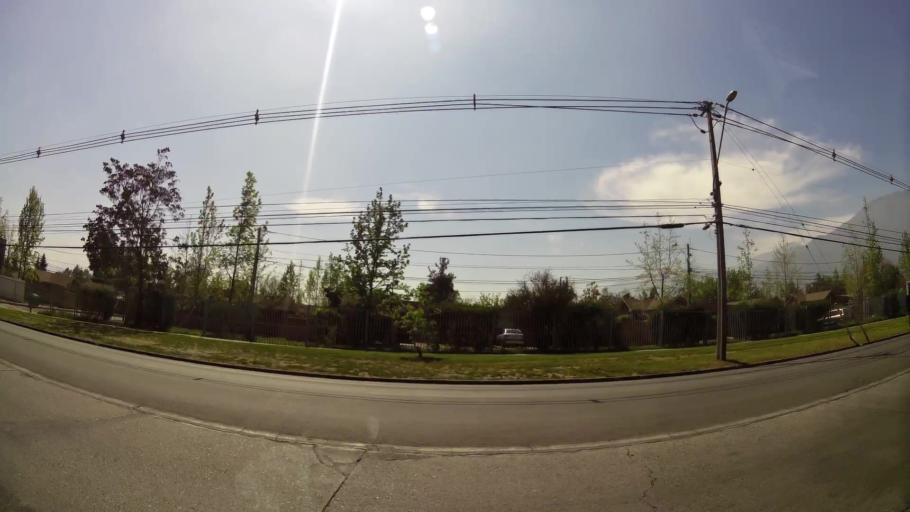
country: CL
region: Santiago Metropolitan
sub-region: Provincia de Santiago
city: Villa Presidente Frei, Nunoa, Santiago, Chile
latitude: -33.4640
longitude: -70.5367
